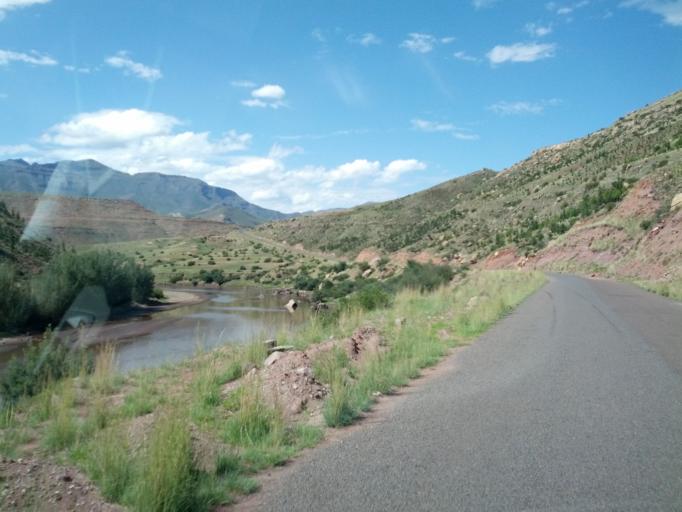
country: LS
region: Qacha's Nek
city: Qacha's Nek
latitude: -30.0746
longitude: 28.4544
